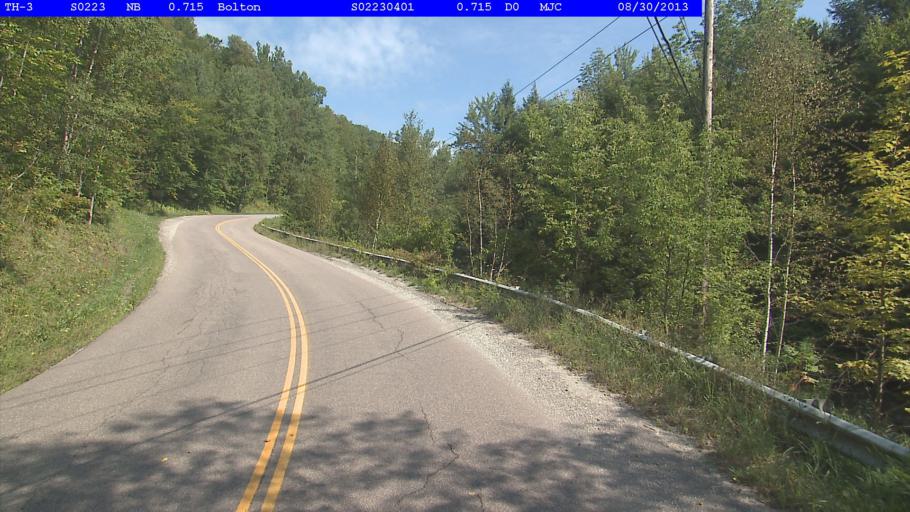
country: US
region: Vermont
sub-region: Washington County
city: Waterbury
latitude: 44.3811
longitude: -72.8751
